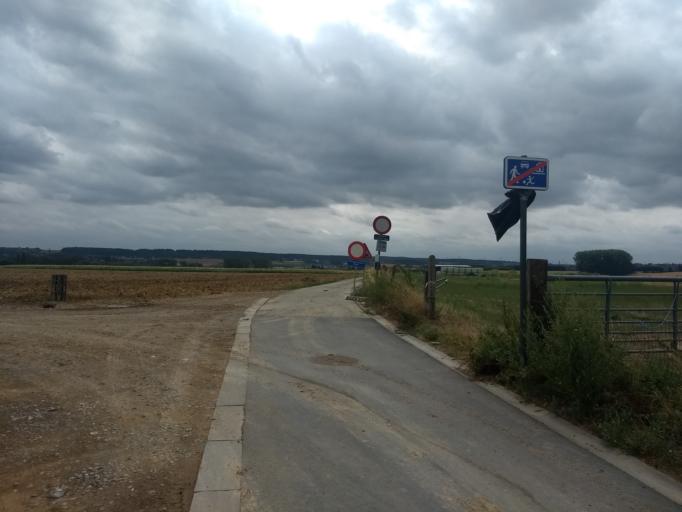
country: BE
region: Wallonia
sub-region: Province du Brabant Wallon
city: Tubize
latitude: 50.7163
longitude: 4.2022
